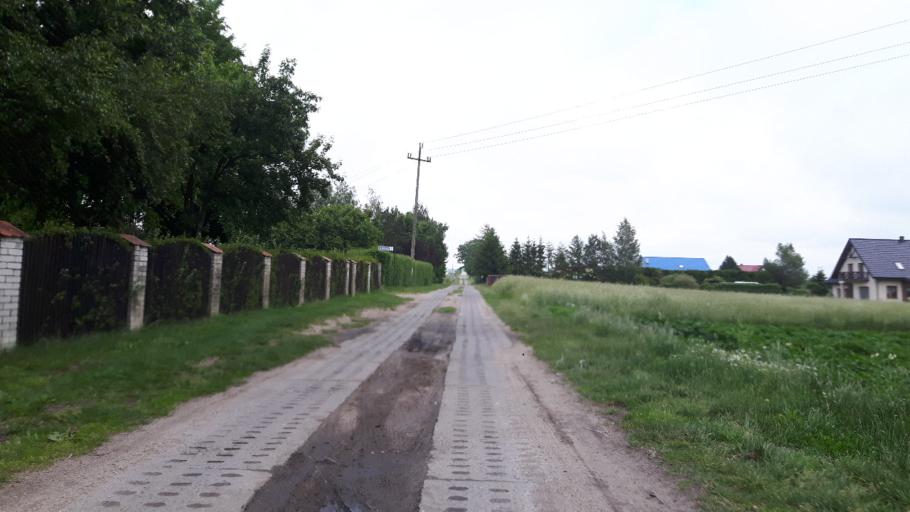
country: PL
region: West Pomeranian Voivodeship
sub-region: Powiat koszalinski
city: Sianow
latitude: 54.2829
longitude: 16.2183
